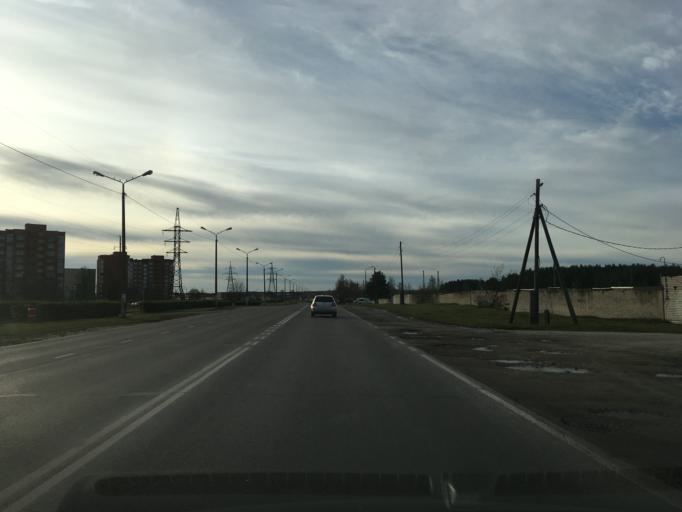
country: EE
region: Ida-Virumaa
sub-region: Narva linn
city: Narva
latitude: 59.3833
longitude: 28.1591
